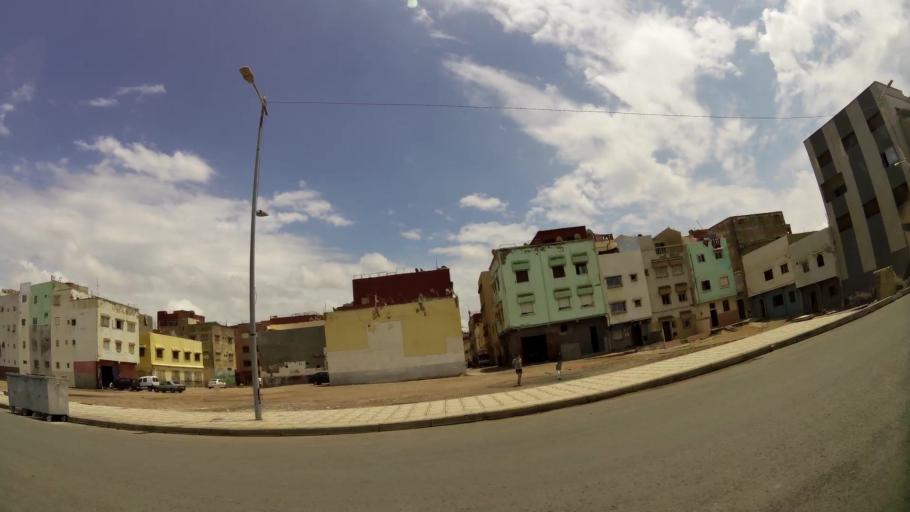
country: MA
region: Rabat-Sale-Zemmour-Zaer
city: Sale
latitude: 34.0505
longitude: -6.8261
